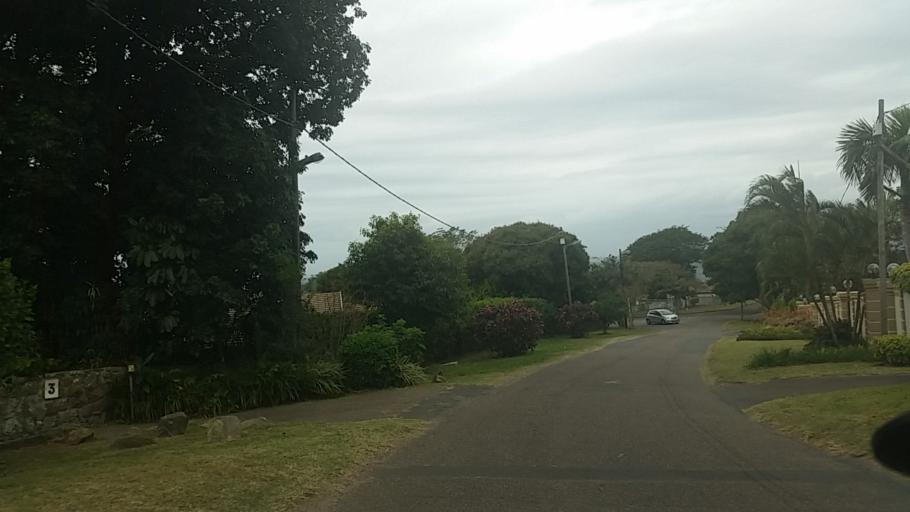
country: ZA
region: KwaZulu-Natal
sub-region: eThekwini Metropolitan Municipality
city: Berea
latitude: -29.8437
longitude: 30.9340
